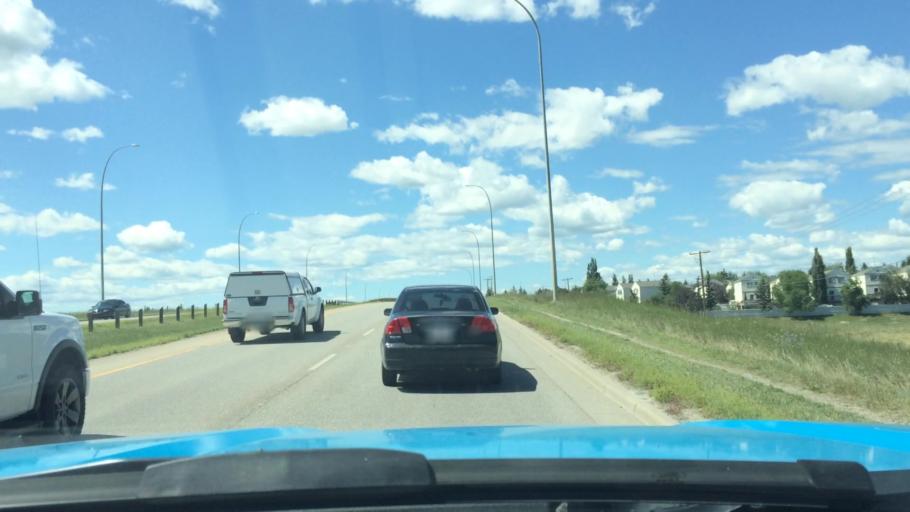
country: CA
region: Alberta
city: Calgary
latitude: 51.1541
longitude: -114.0377
